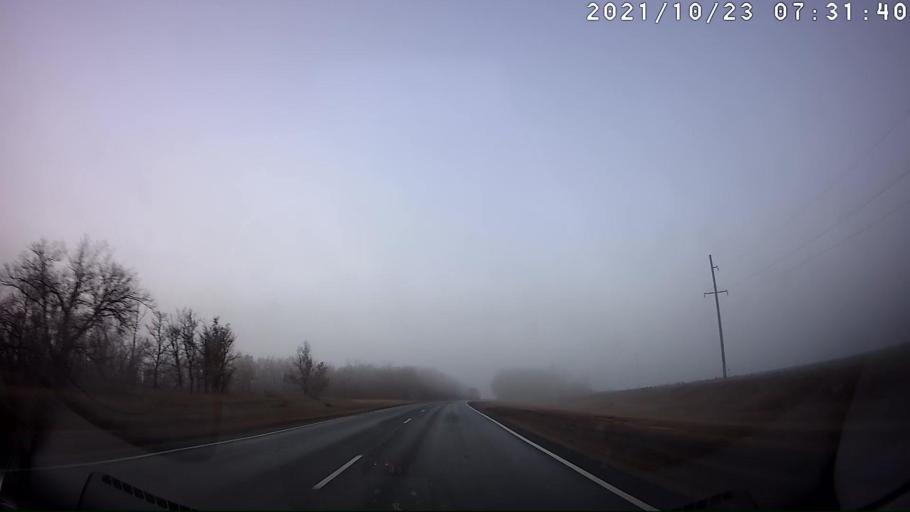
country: RU
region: Saratov
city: Alekseyevka
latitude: 52.2765
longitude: 47.9313
